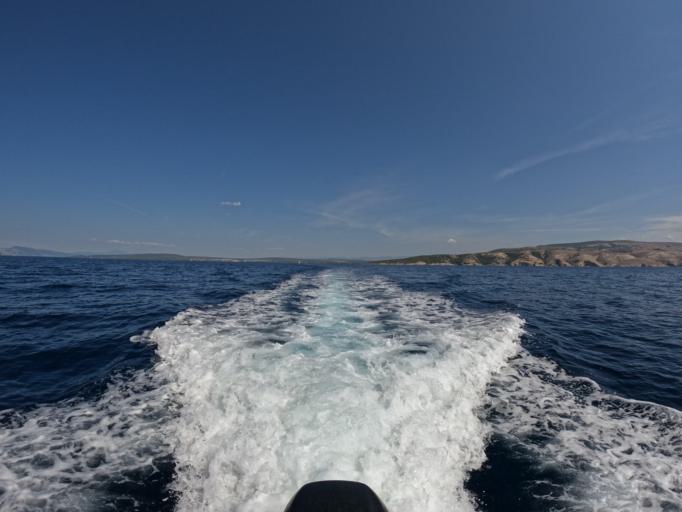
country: HR
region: Primorsko-Goranska
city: Punat
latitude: 44.9522
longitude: 14.6119
